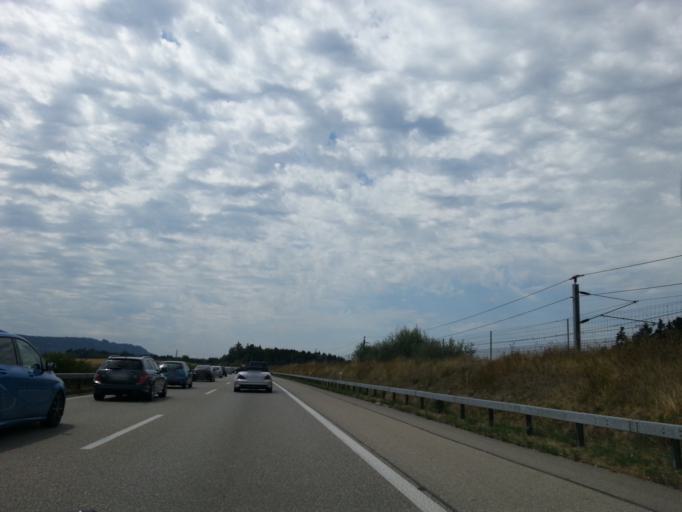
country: CH
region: Bern
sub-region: Emmental District
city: Hindelbank
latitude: 47.0503
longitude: 7.5345
